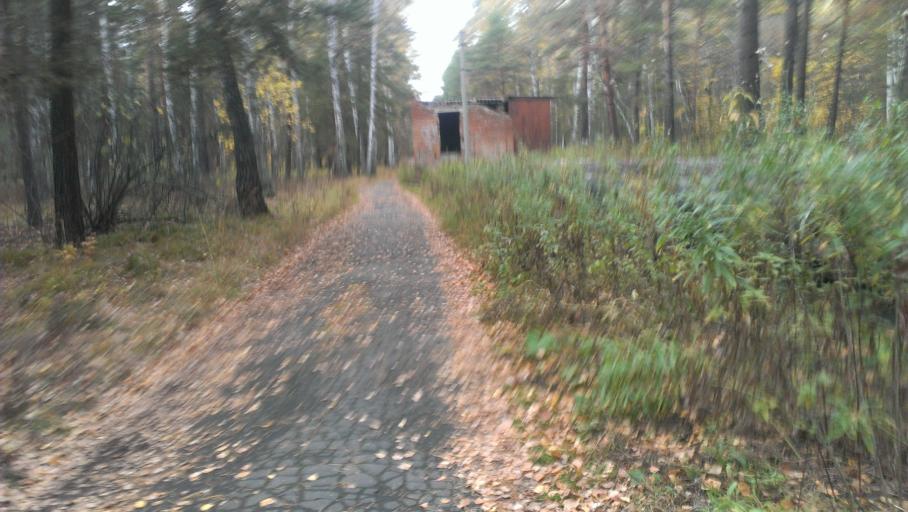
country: RU
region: Altai Krai
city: Yuzhnyy
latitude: 53.2690
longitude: 83.6818
